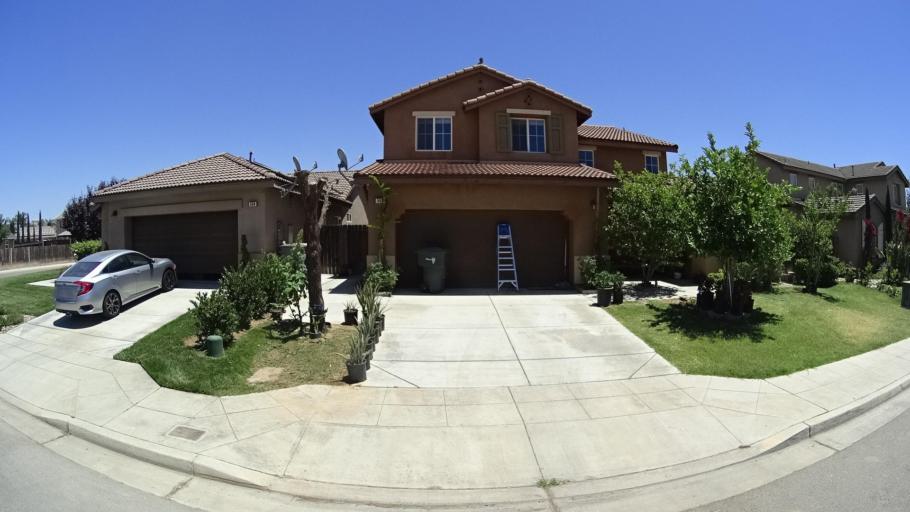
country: US
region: California
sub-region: Fresno County
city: Sunnyside
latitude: 36.7280
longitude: -119.6671
